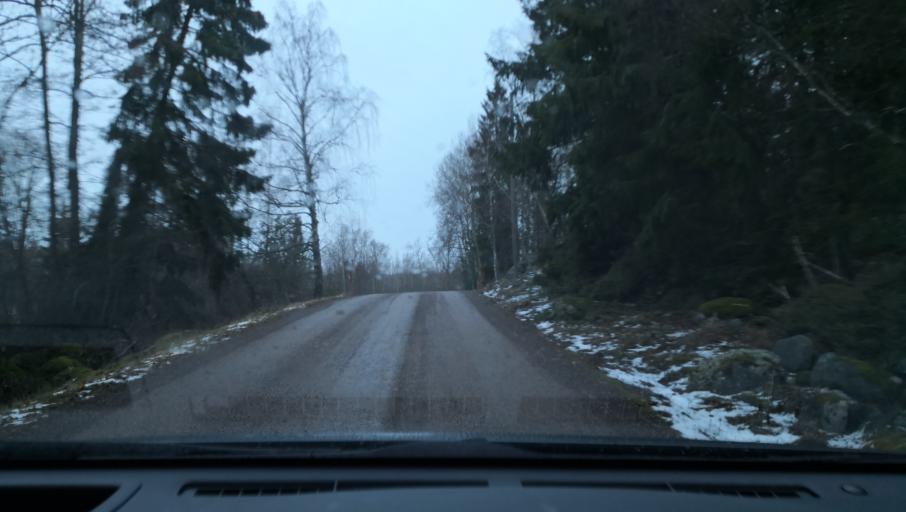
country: SE
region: Uppsala
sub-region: Enkopings Kommun
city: Hummelsta
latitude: 59.4604
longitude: 16.8430
